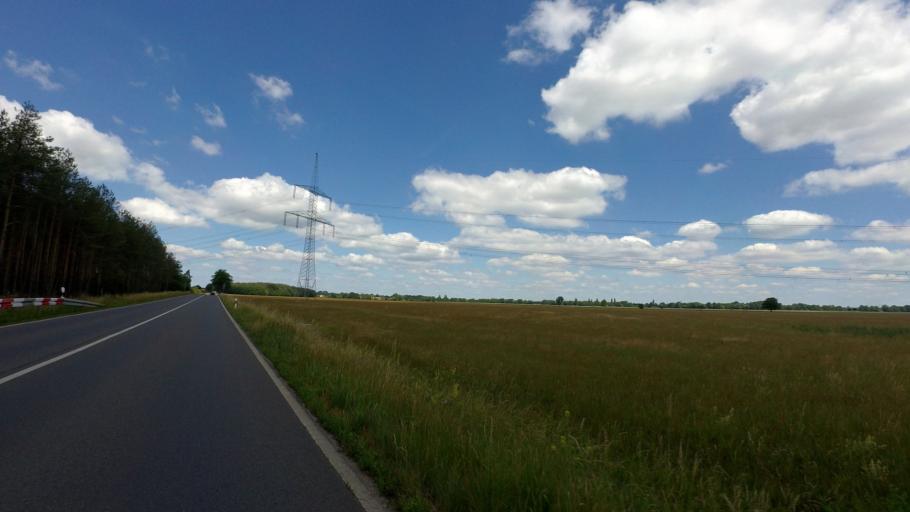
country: DE
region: Brandenburg
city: Sonnewalde
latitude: 51.6582
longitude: 13.6582
